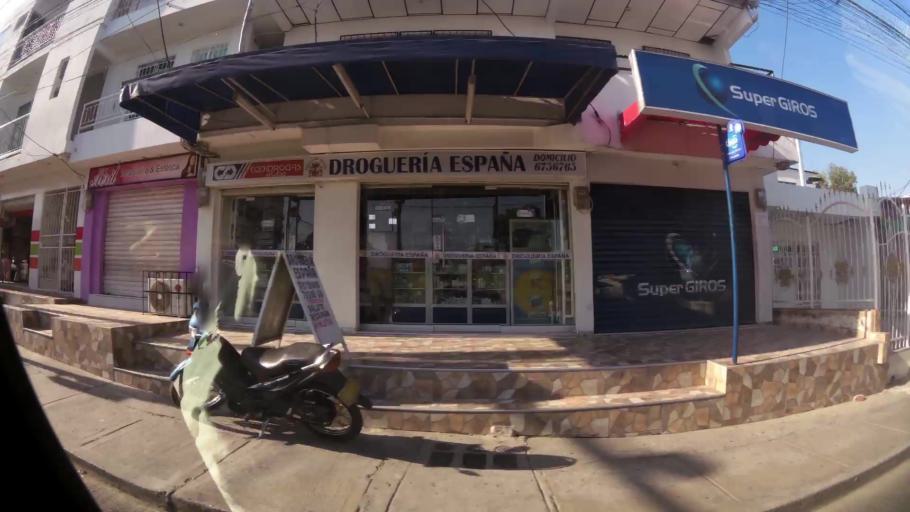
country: CO
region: Bolivar
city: Cartagena
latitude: 10.4003
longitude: -75.5014
